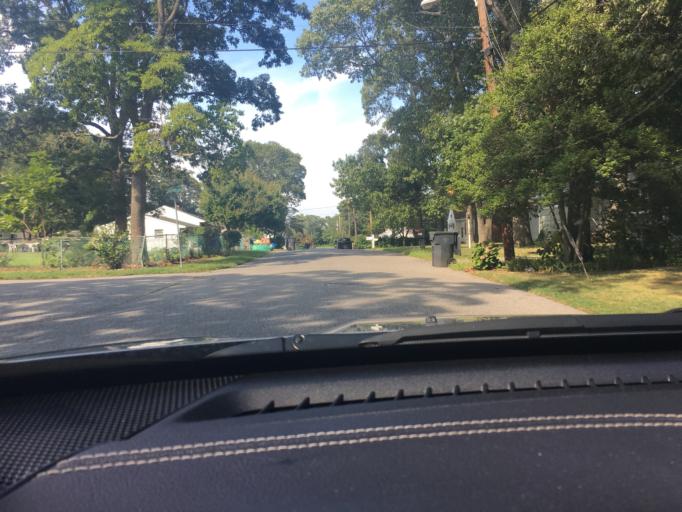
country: US
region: New Jersey
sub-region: Ocean County
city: Leisure Village East
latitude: 40.0536
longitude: -74.1259
